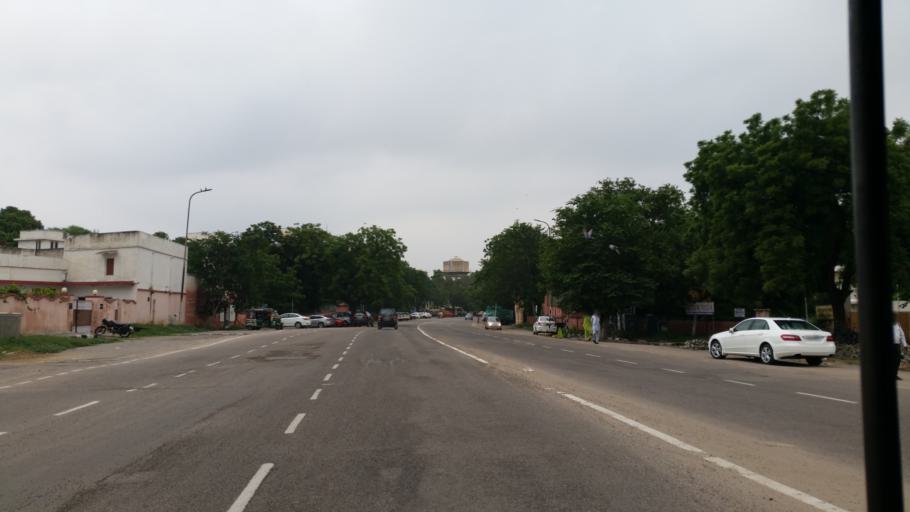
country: IN
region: Rajasthan
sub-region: Jaipur
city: Jaipur
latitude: 26.9116
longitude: 75.7882
